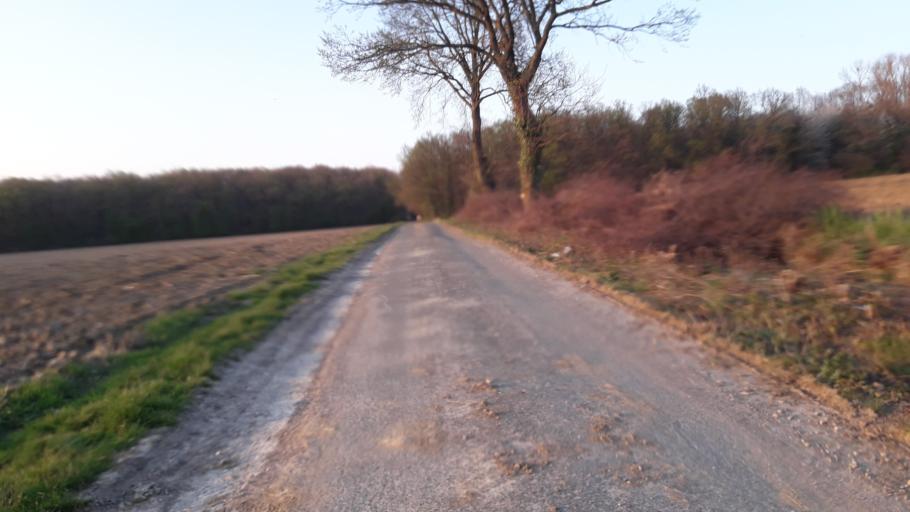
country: DE
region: North Rhine-Westphalia
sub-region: Regierungsbezirk Detmold
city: Salzkotten
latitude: 51.6644
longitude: 8.6481
